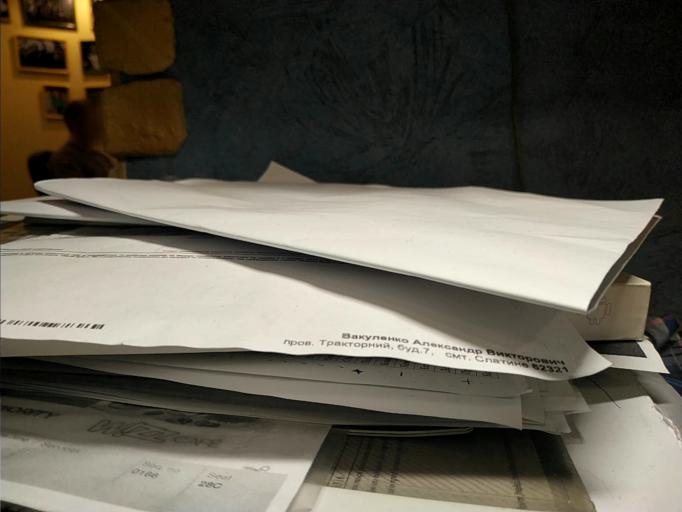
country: RU
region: Tverskaya
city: Zubtsov
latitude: 56.1076
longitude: 34.6453
